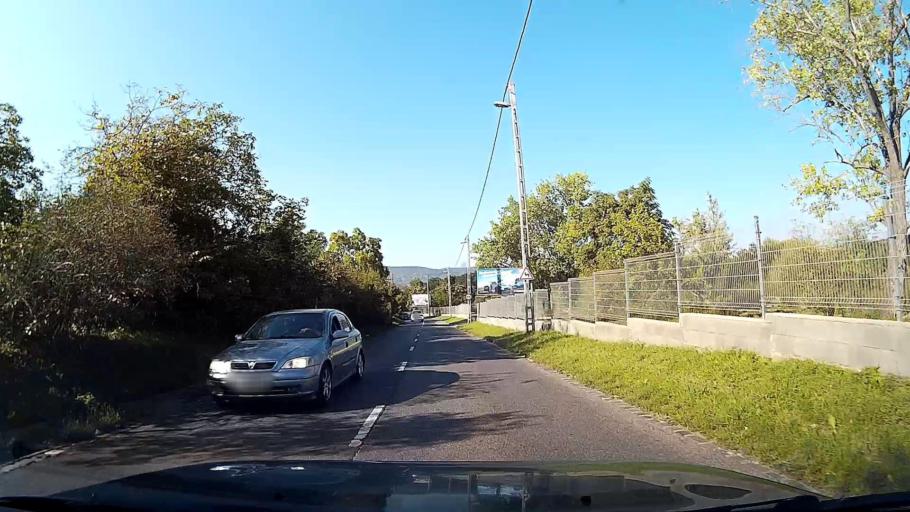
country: HU
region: Pest
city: Budaors
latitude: 47.4345
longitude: 18.9795
